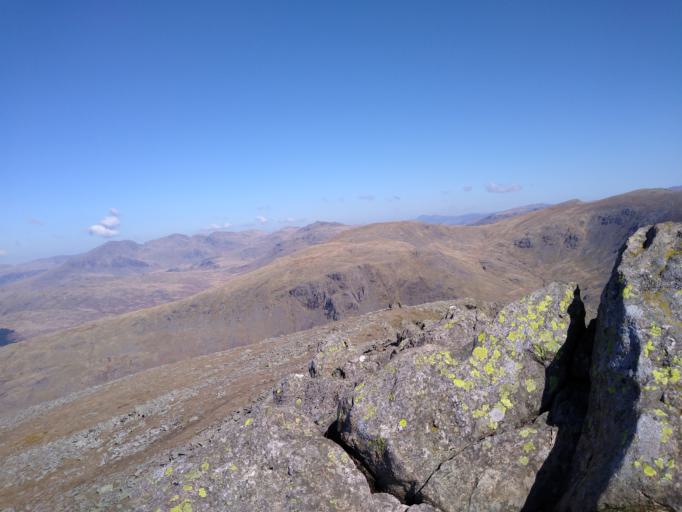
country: GB
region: England
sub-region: Cumbria
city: Ulverston
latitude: 54.3703
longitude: -3.1367
